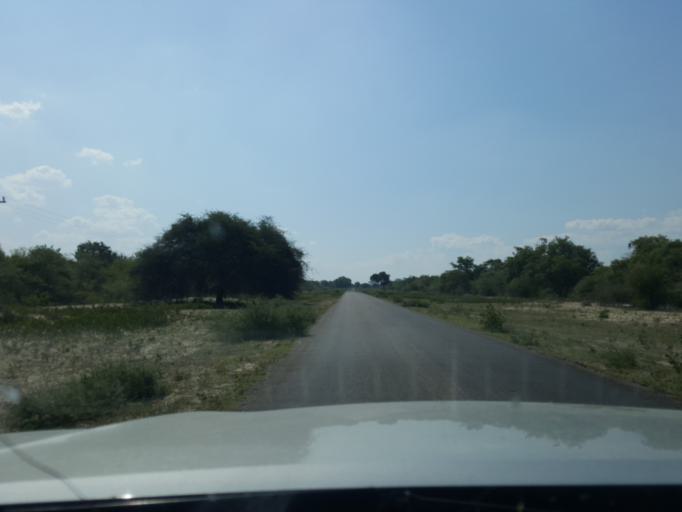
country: BW
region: North West
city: Shakawe
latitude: -18.7882
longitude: 22.1963
